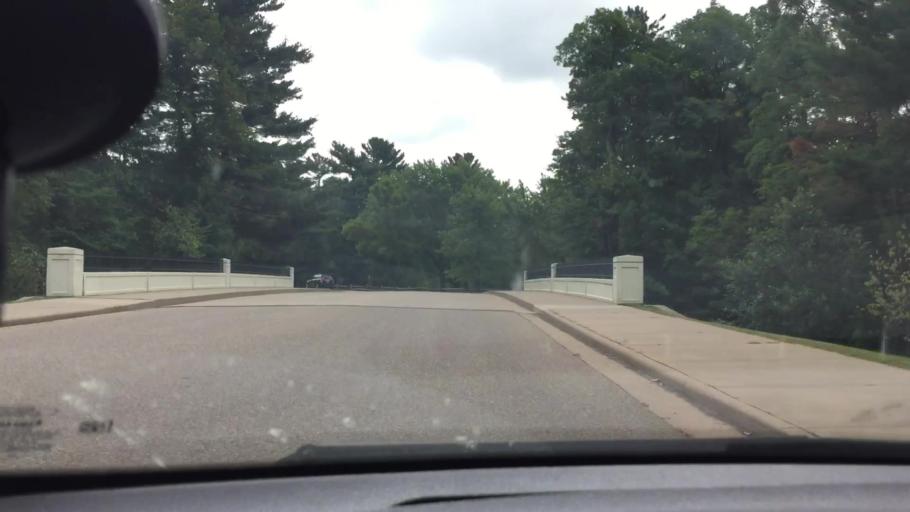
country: US
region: Wisconsin
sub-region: Chippewa County
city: Chippewa Falls
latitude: 44.9477
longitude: -91.4007
